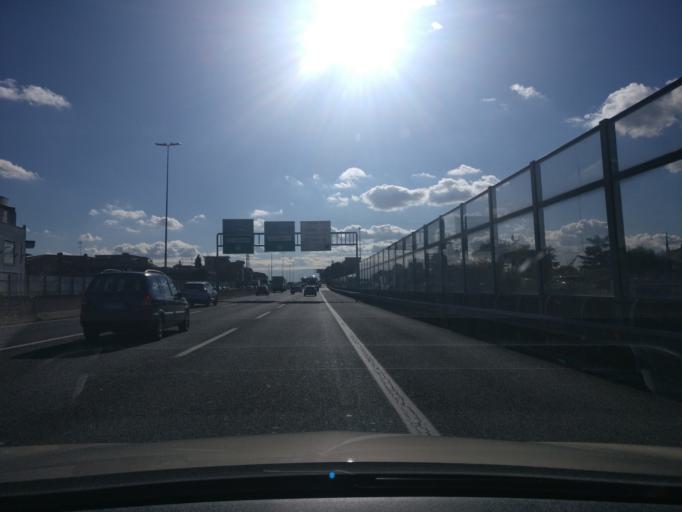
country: IT
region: Latium
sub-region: Citta metropolitana di Roma Capitale
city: Ciampino
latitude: 41.8440
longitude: 12.5936
